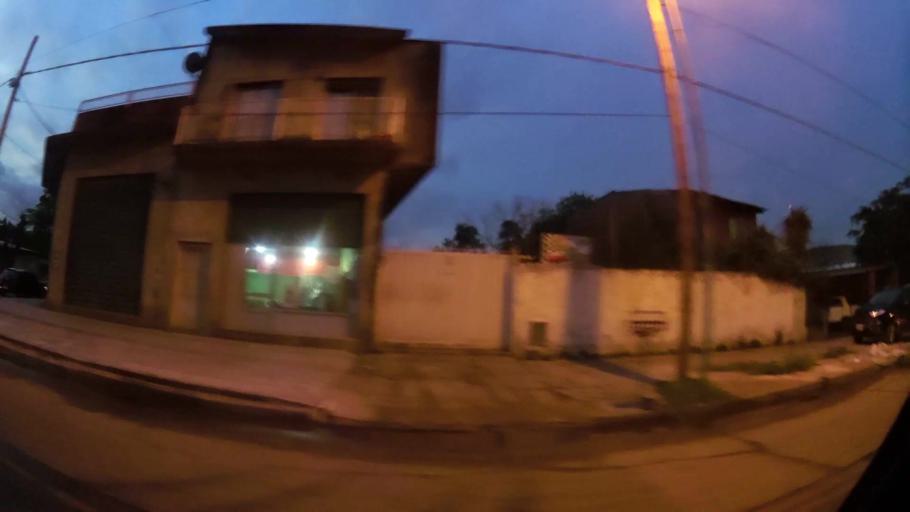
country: AR
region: Buenos Aires
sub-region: Partido de Lomas de Zamora
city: Lomas de Zamora
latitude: -34.7432
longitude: -58.3623
